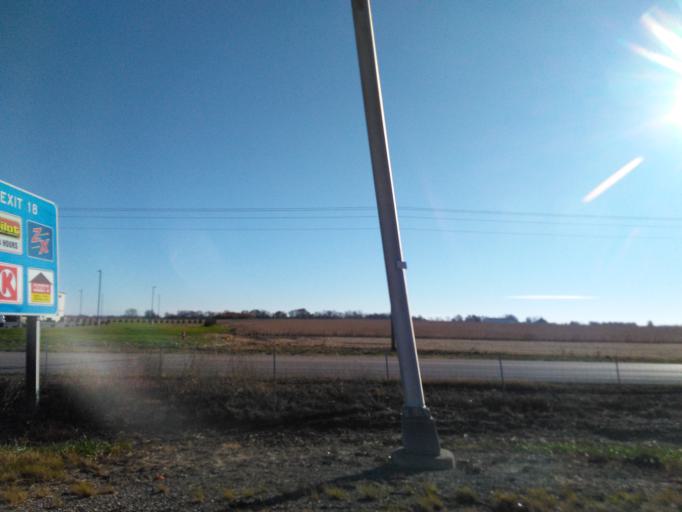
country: US
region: Illinois
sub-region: Madison County
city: Troy
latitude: 38.7275
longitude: -89.9138
